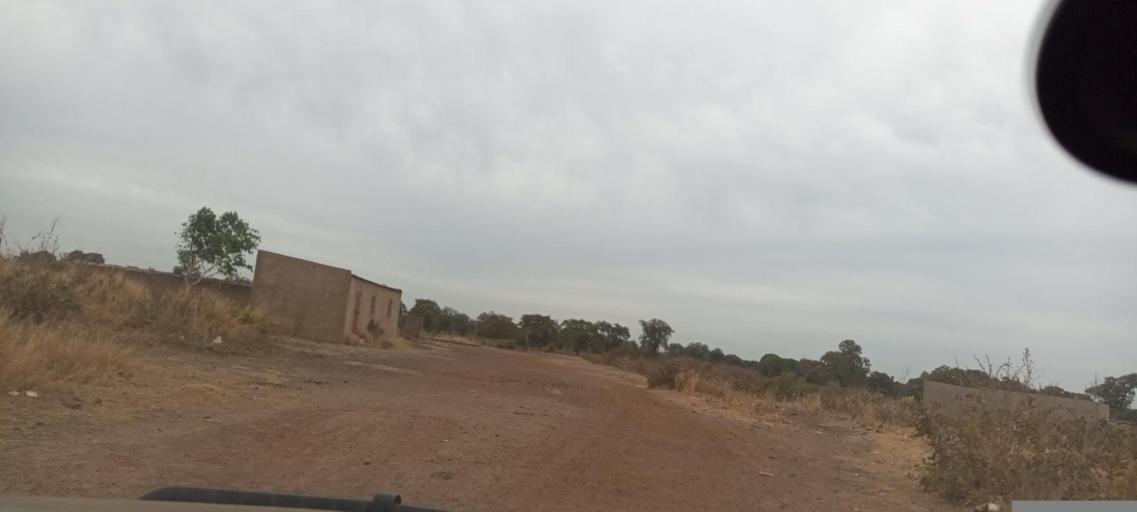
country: ML
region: Koulikoro
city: Kati
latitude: 12.7962
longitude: -8.2510
